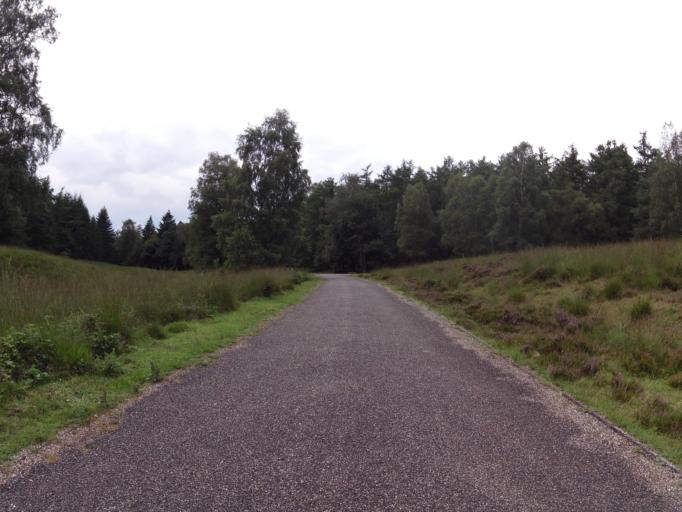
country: NL
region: Gelderland
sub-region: Gemeente Apeldoorn
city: Loenen
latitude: 52.0902
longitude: 5.9676
